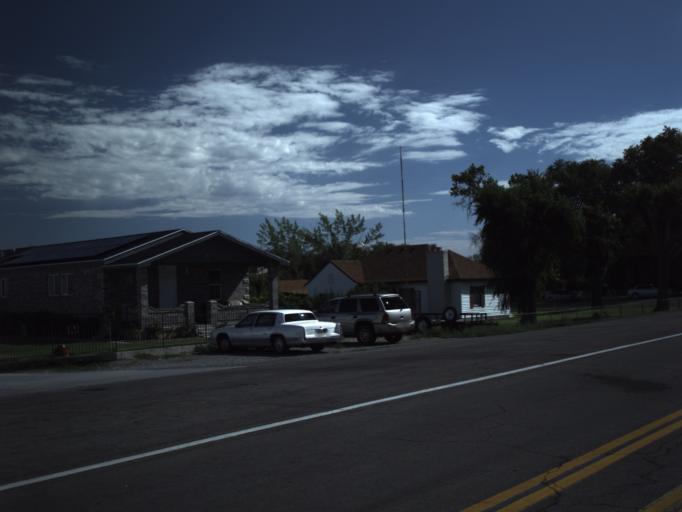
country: US
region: Utah
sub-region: Utah County
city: Genola
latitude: 39.9528
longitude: -111.9041
